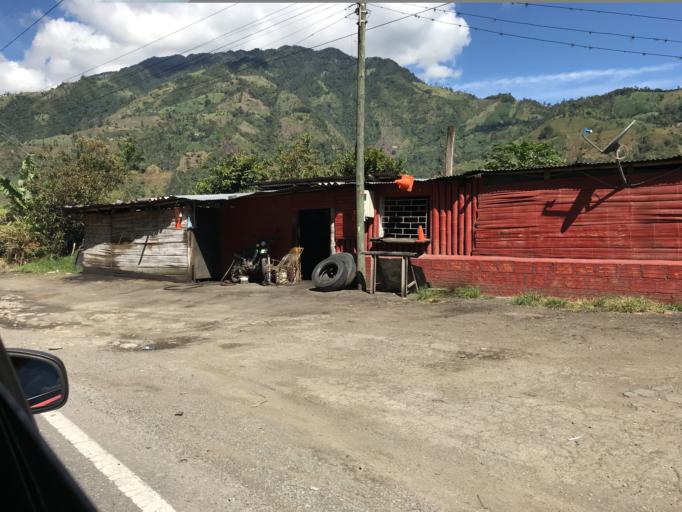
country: CO
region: Tolima
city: Cajamarca
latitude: 4.4426
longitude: -75.4074
